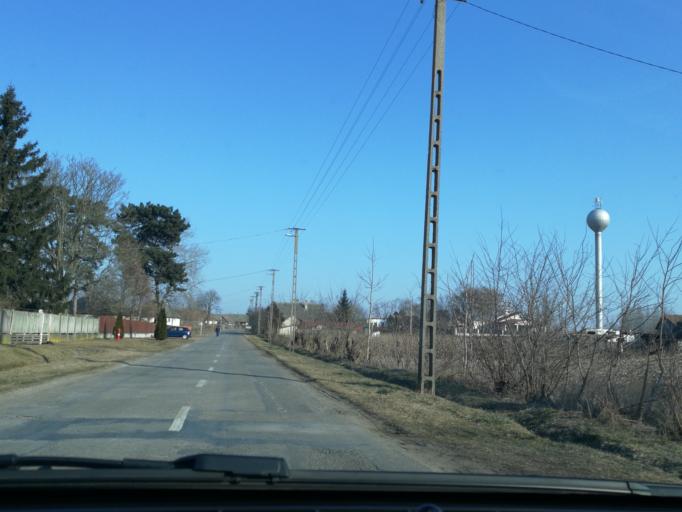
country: HU
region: Szabolcs-Szatmar-Bereg
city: Nyirbogdany
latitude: 48.0535
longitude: 21.9358
